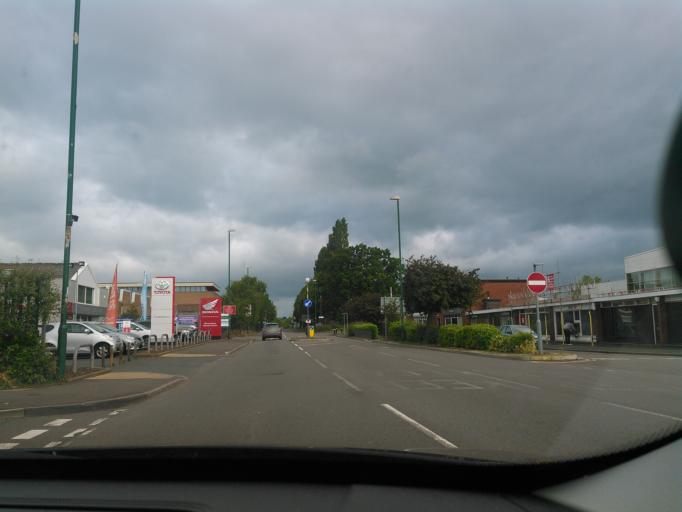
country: GB
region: England
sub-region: Shropshire
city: Shrewsbury
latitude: 52.7369
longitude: -2.7254
